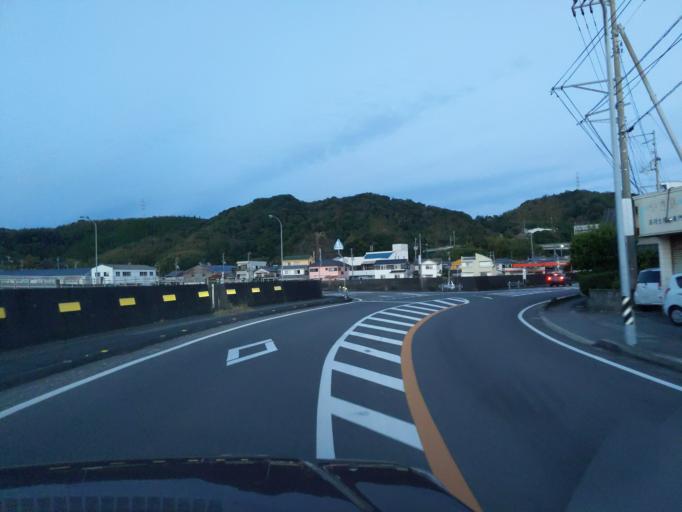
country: JP
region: Tokushima
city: Anan
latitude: 33.8721
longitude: 134.6385
